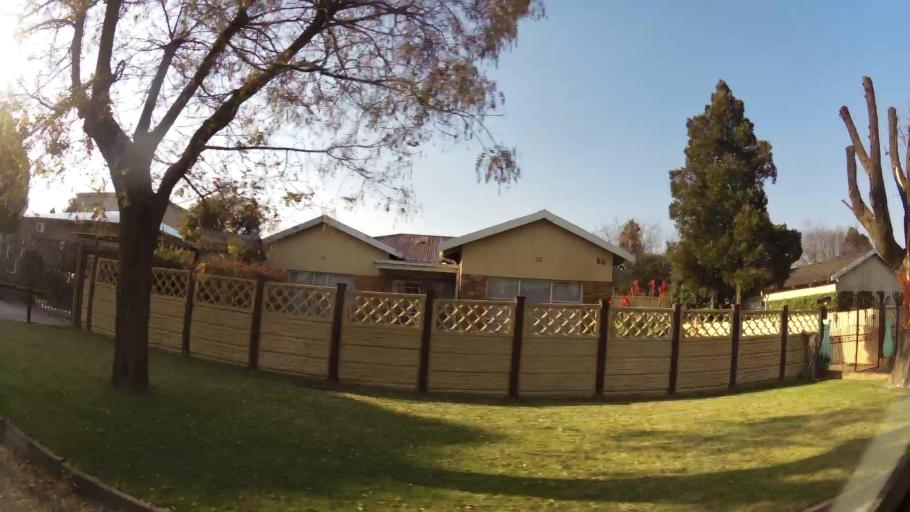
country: ZA
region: Gauteng
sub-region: Ekurhuleni Metropolitan Municipality
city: Springs
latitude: -26.2554
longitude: 28.3828
